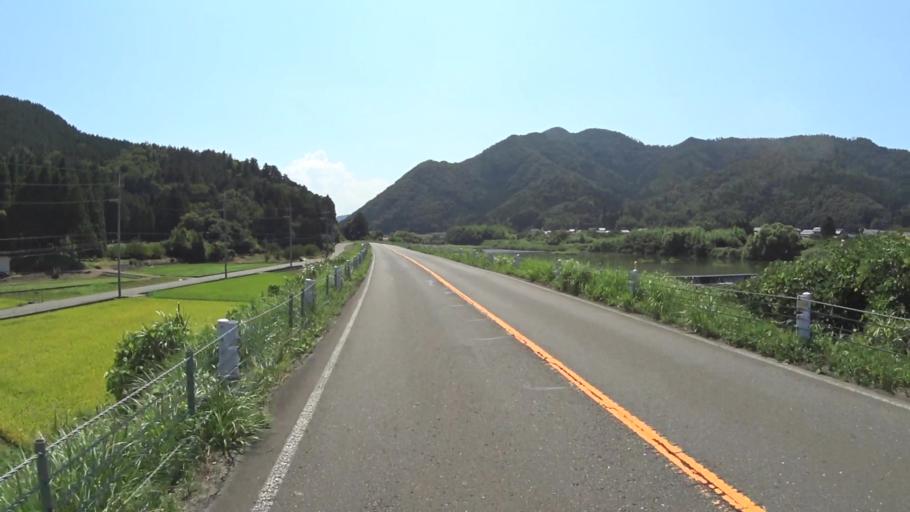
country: JP
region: Fukui
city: Obama
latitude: 35.4707
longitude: 135.7339
